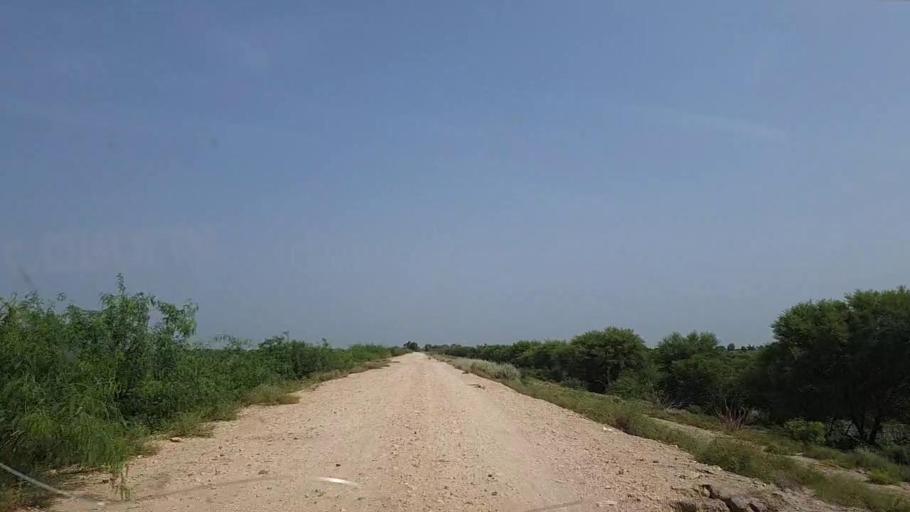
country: PK
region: Sindh
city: Ghotki
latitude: 28.0938
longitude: 69.4066
